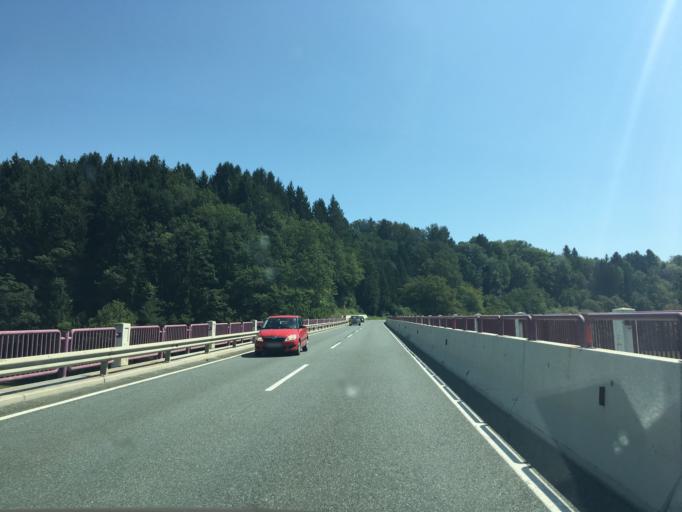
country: AT
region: Carinthia
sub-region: Politischer Bezirk Volkermarkt
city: Voelkermarkt
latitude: 46.6455
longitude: 14.6287
